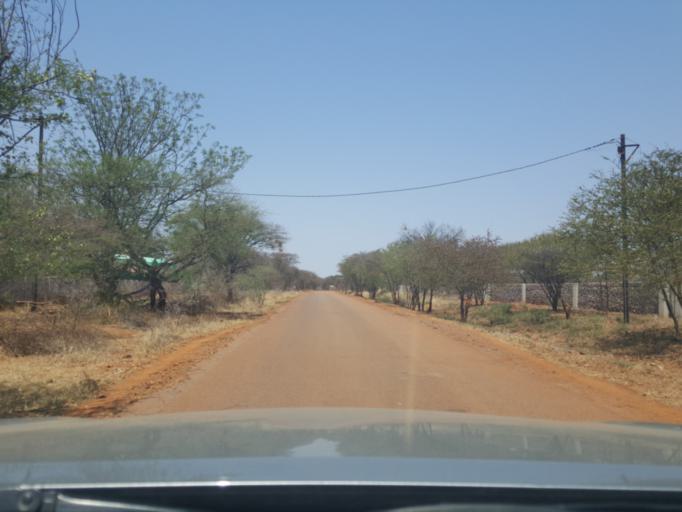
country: BW
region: South East
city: Ramotswa
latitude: -24.7718
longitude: 25.8452
